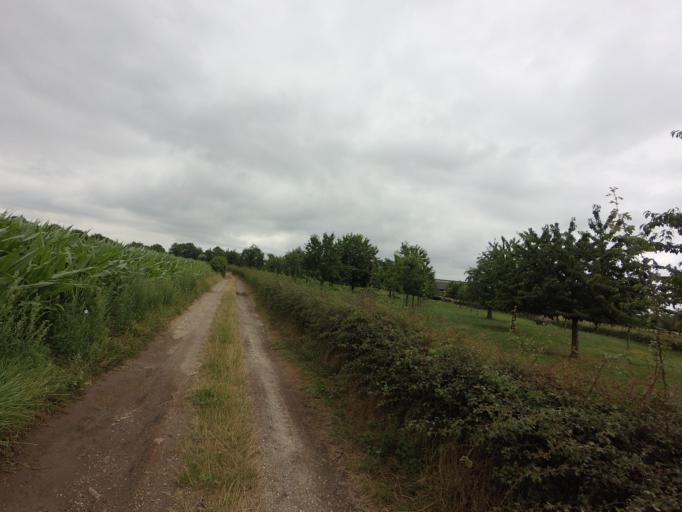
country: NL
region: Limburg
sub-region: Gemeente Maastricht
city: Heer
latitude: 50.8104
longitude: 5.7597
